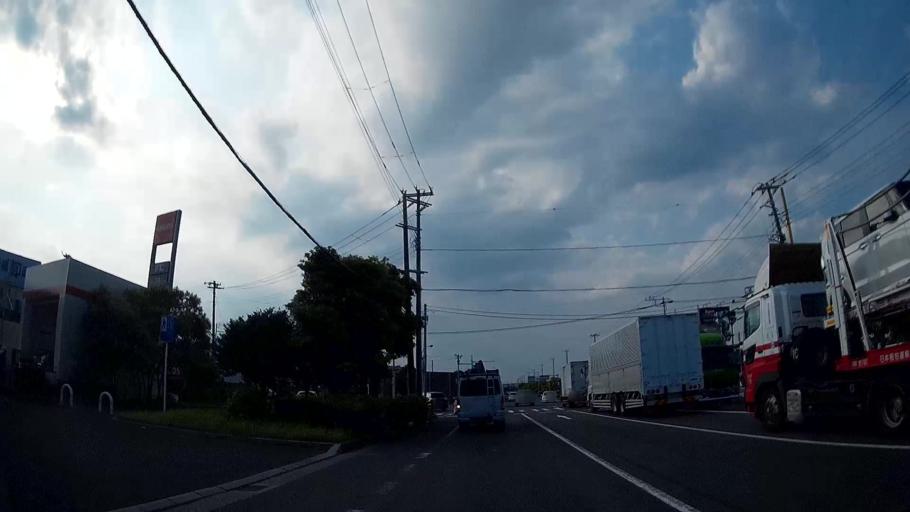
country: JP
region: Chiba
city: Funabashi
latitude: 35.6749
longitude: 140.0001
